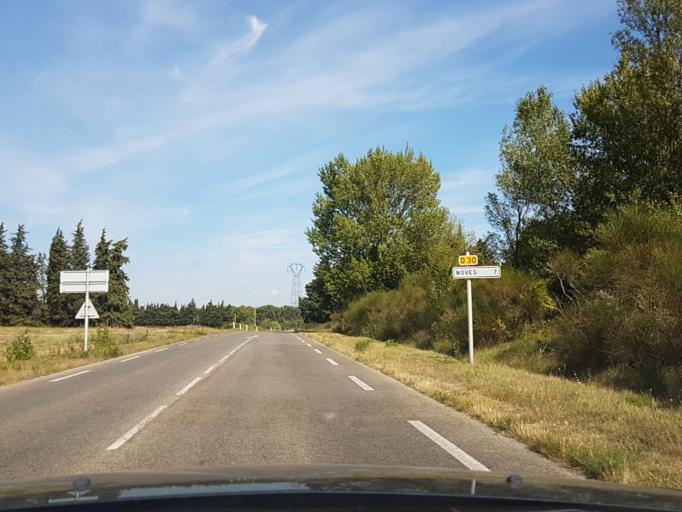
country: FR
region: Provence-Alpes-Cote d'Azur
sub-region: Departement des Bouches-du-Rhone
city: Eyragues
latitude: 43.8222
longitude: 4.8818
